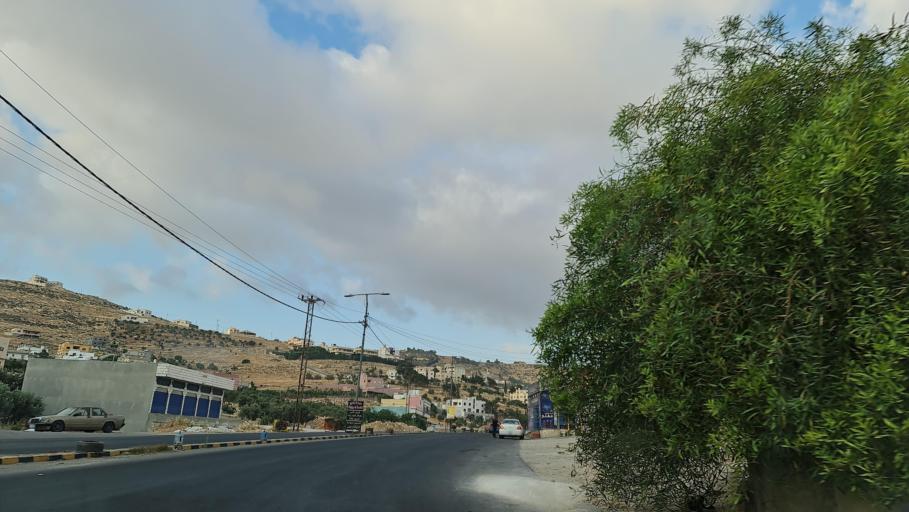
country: JO
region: Amman
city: Al Jubayhah
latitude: 32.0961
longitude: 35.9560
